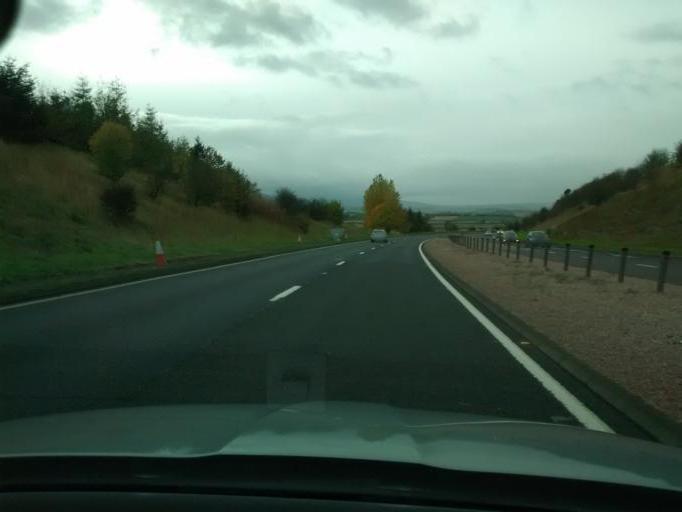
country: GB
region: Scotland
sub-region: Perth and Kinross
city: Methven
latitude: 56.3453
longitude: -3.5822
